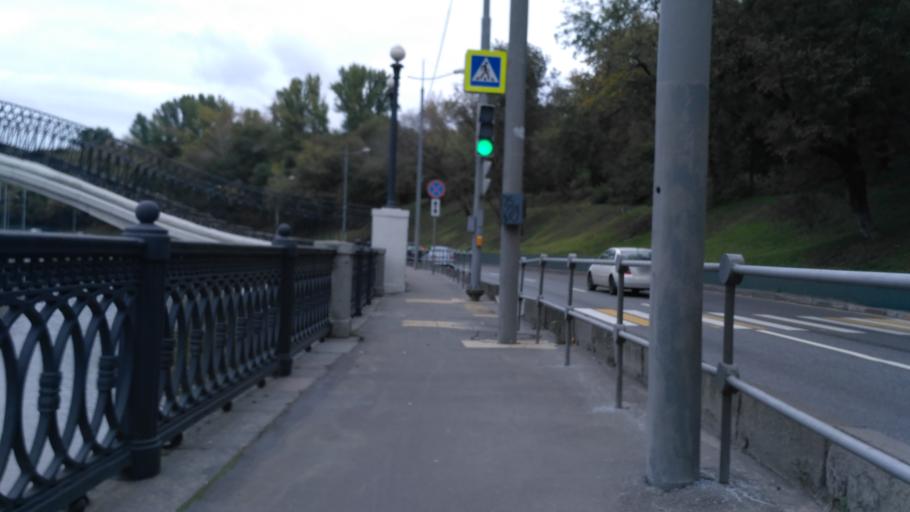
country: RU
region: Moscow
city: Taganskiy
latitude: 55.7523
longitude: 37.6727
